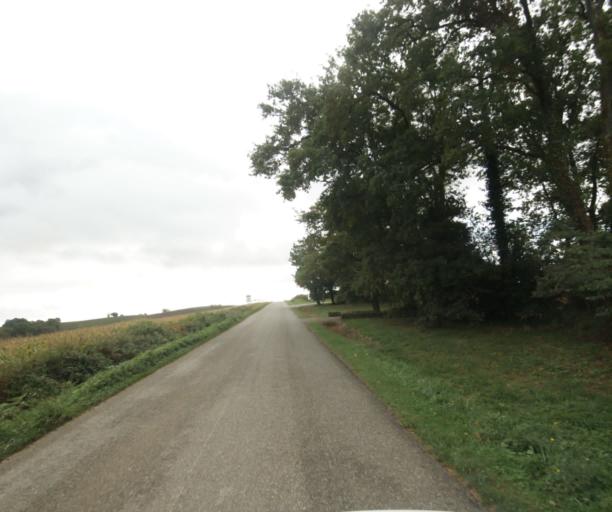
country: FR
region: Midi-Pyrenees
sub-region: Departement du Gers
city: Nogaro
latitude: 43.8317
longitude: -0.0432
